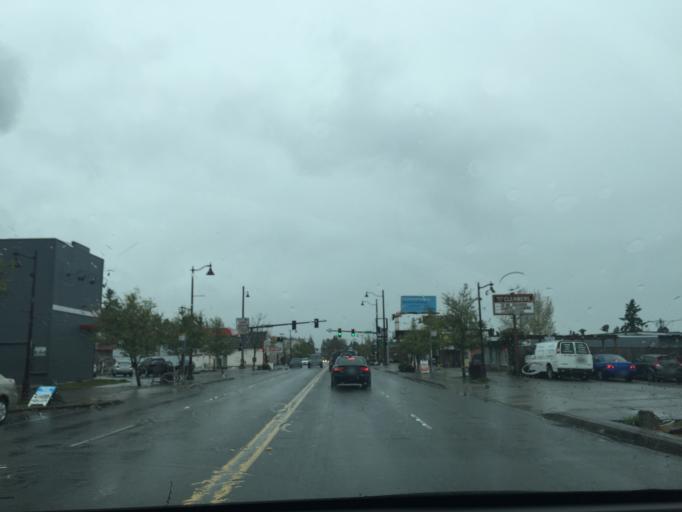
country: US
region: Washington
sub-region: King County
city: Shoreline
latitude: 47.7586
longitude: -122.3135
